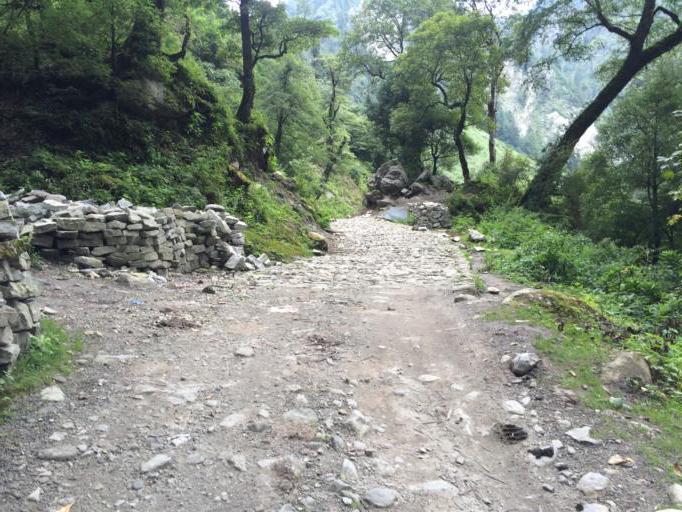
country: NP
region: Western Region
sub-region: Gandaki Zone
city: Chame
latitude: 28.5279
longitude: 84.3186
